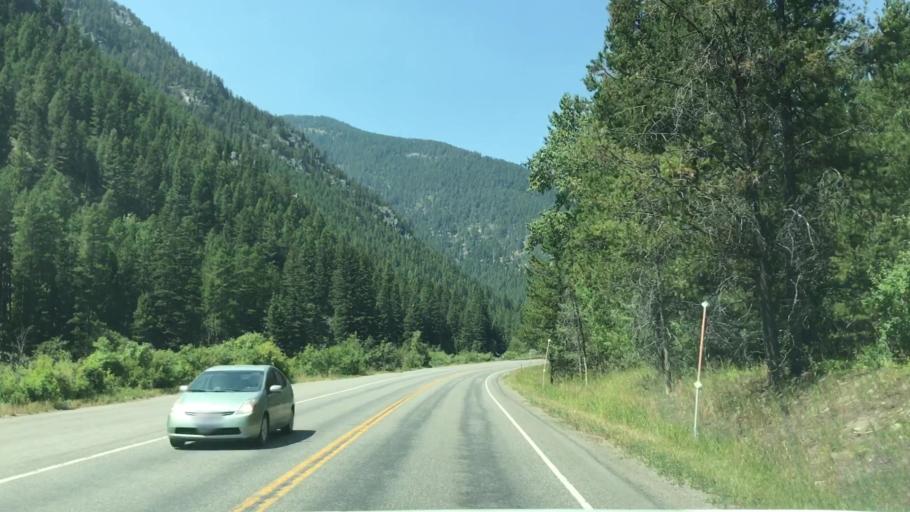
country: US
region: Montana
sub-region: Gallatin County
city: Big Sky
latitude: 45.3958
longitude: -111.2088
